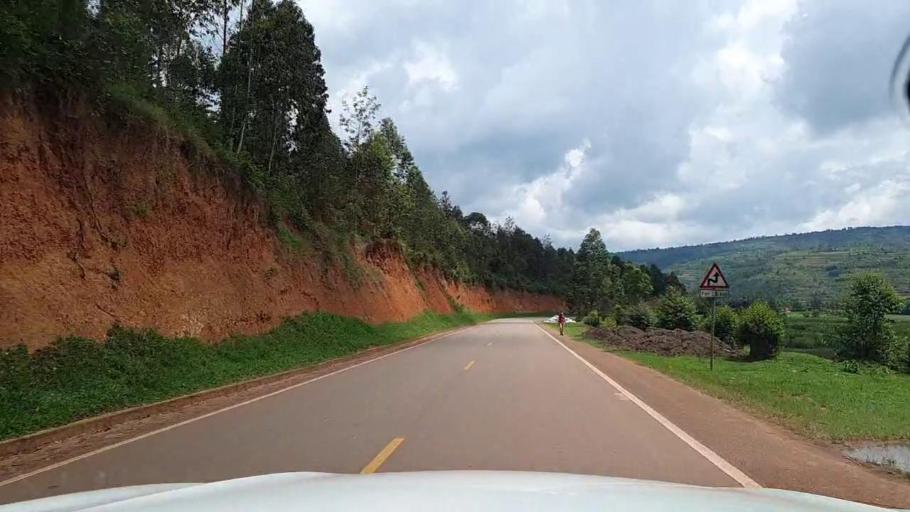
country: RW
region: Kigali
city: Kigali
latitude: -1.8123
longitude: 30.1204
